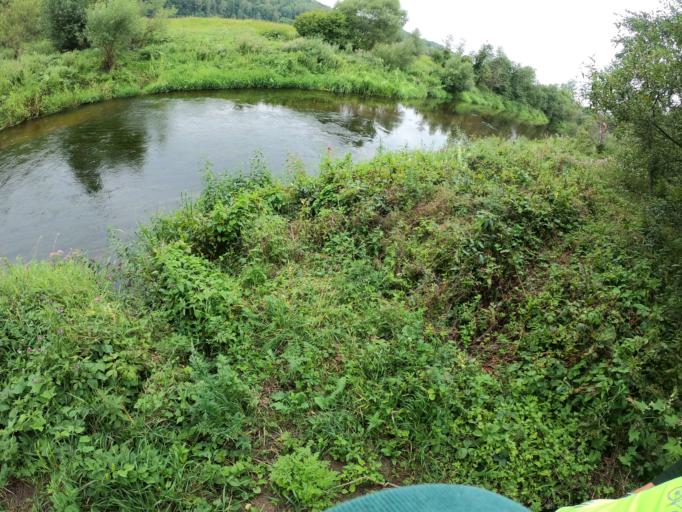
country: LT
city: Raseiniai
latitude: 55.3804
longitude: 23.2835
